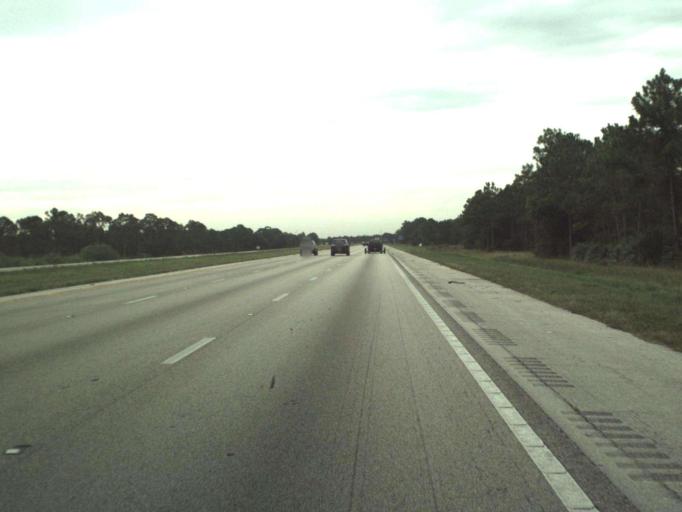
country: US
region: Florida
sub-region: Martin County
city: Palm City
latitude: 27.1374
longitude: -80.3637
